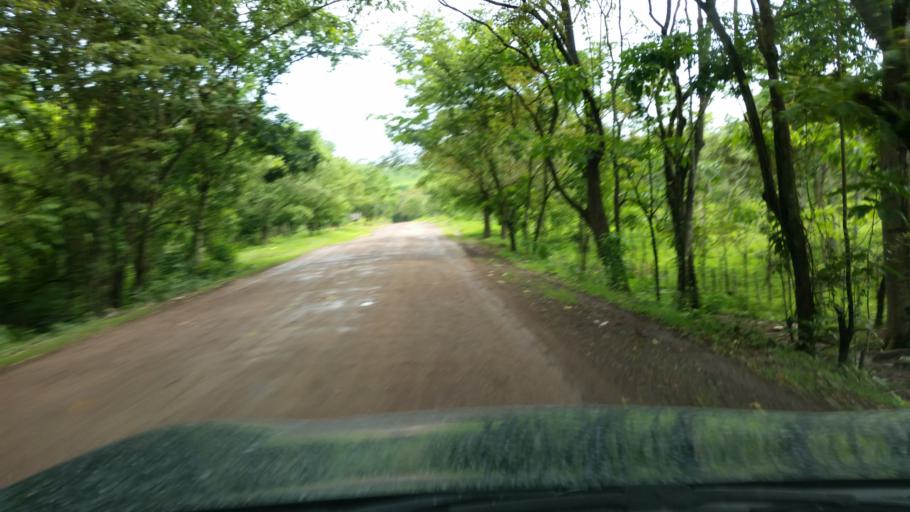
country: NI
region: Atlantico Norte (RAAN)
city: Siuna
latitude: 13.5101
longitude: -84.8426
